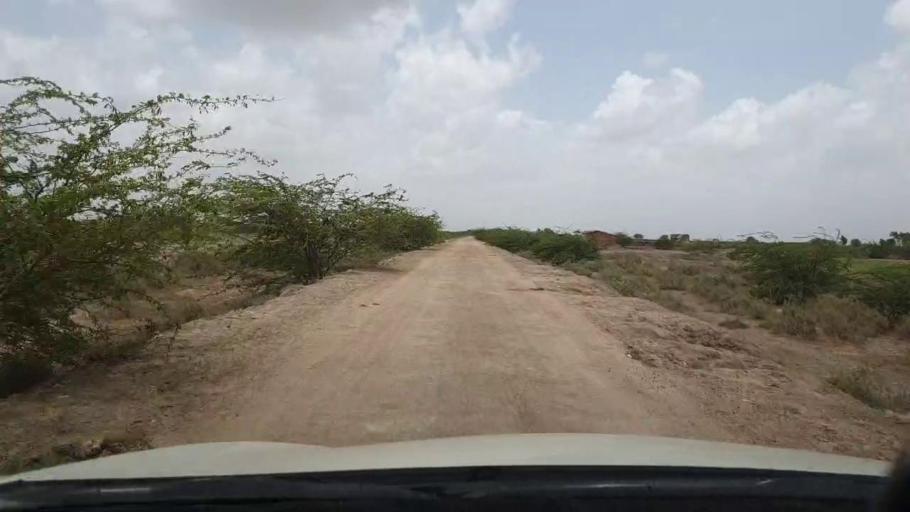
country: PK
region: Sindh
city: Kadhan
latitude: 24.3603
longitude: 68.9365
